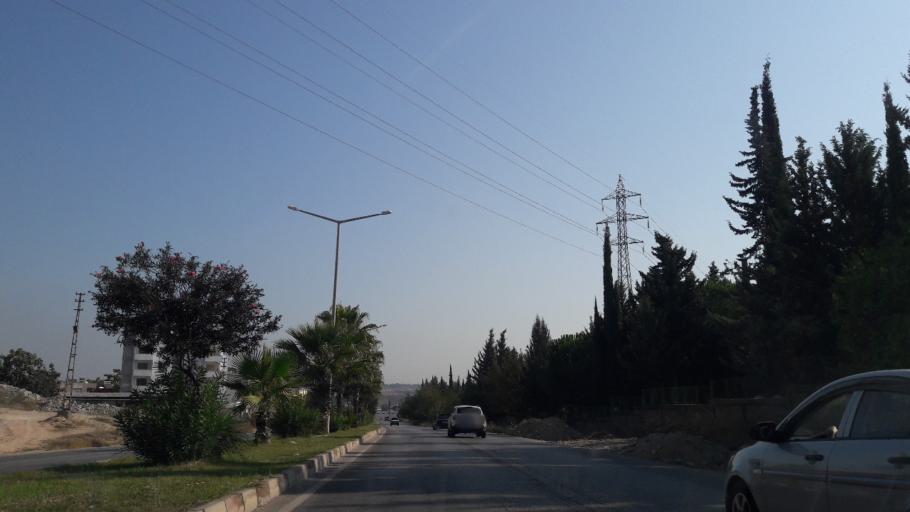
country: TR
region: Adana
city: Yuregir
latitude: 37.0430
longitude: 35.4318
